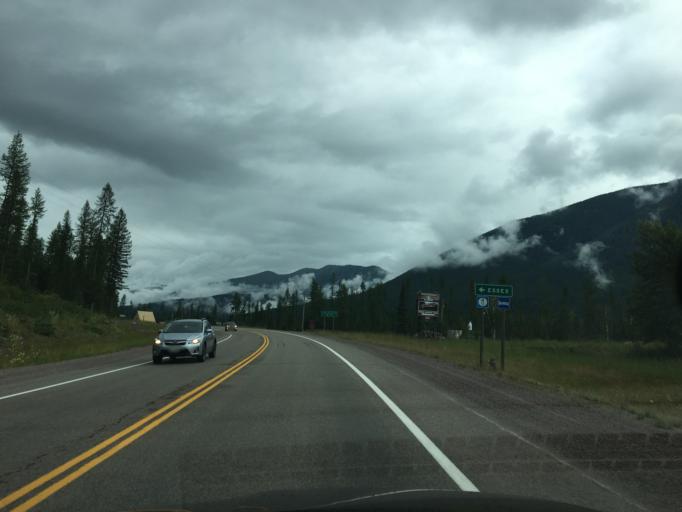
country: US
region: Montana
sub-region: Flathead County
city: Bigfork
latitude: 48.2821
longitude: -113.6066
